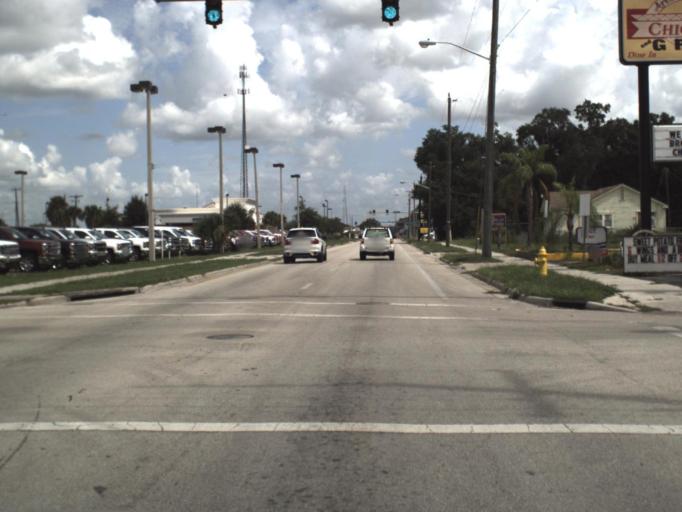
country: US
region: Florida
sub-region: DeSoto County
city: Arcadia
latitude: 27.2118
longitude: -81.8603
